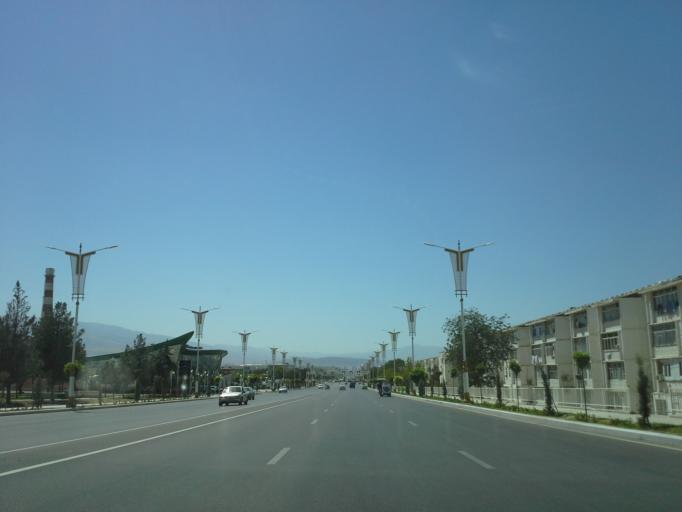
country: TM
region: Ahal
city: Ashgabat
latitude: 37.9100
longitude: 58.4317
